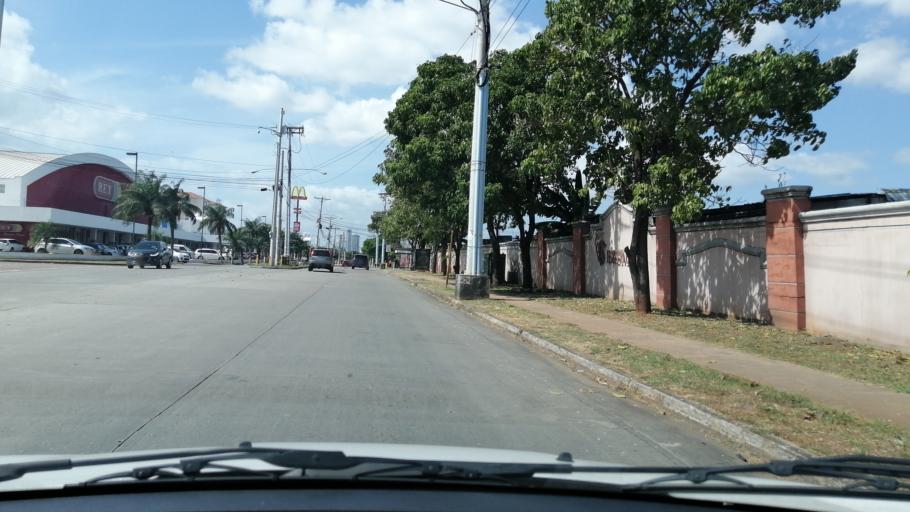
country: PA
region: Panama
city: Tocumen
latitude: 9.0441
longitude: -79.4153
